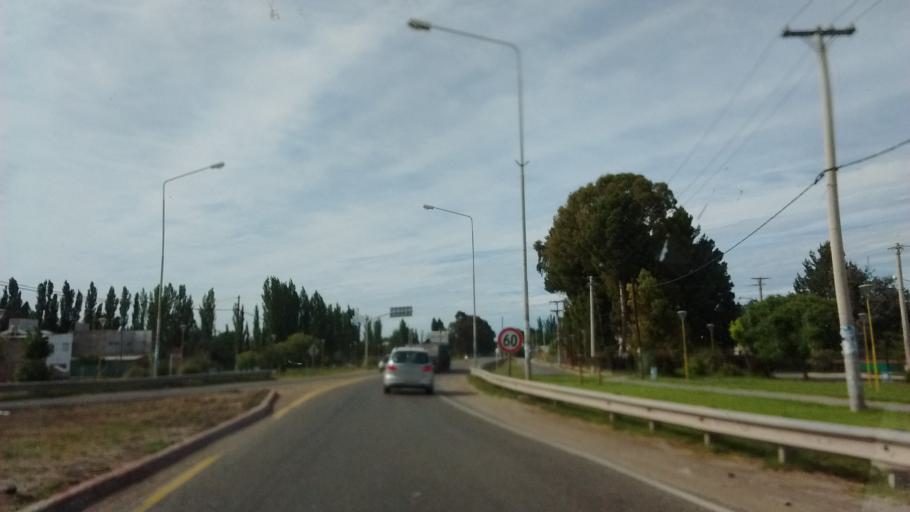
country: AR
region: Neuquen
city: Centenario
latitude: -38.8202
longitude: -68.1344
